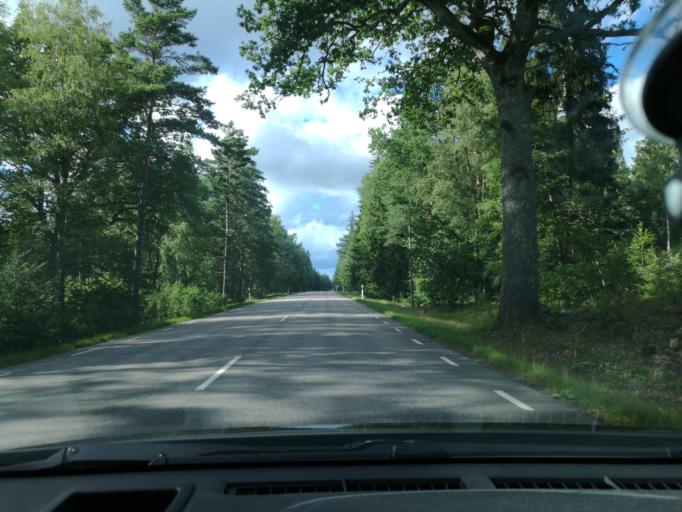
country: SE
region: Kronoberg
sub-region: Vaxjo Kommun
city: Braas
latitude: 57.0490
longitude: 15.0618
